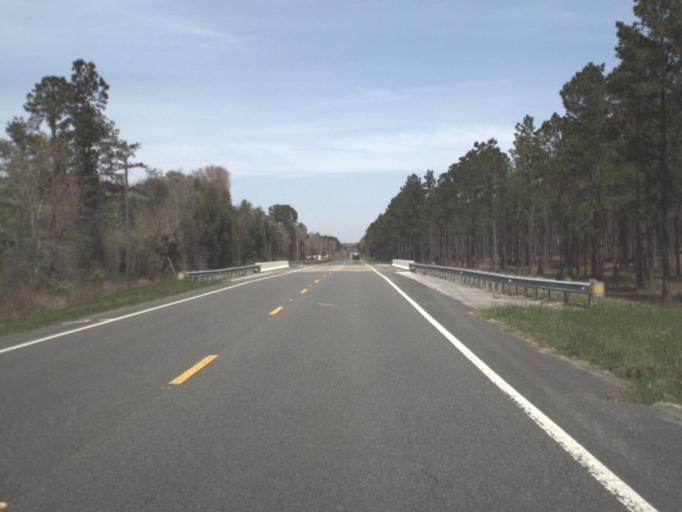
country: US
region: Florida
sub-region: Walton County
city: DeFuniak Springs
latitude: 30.7995
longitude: -85.9584
